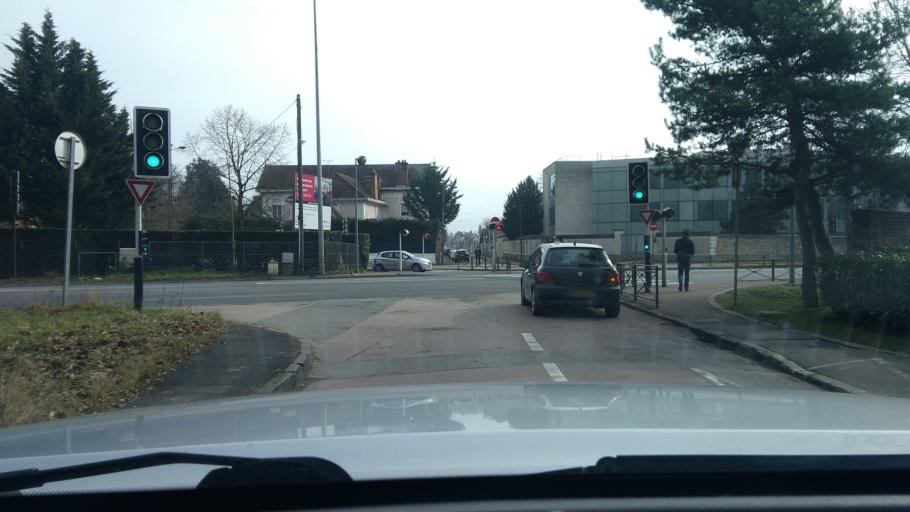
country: FR
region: Ile-de-France
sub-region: Departement de Seine-et-Marne
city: Fontainebleau
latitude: 48.4057
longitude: 2.6864
